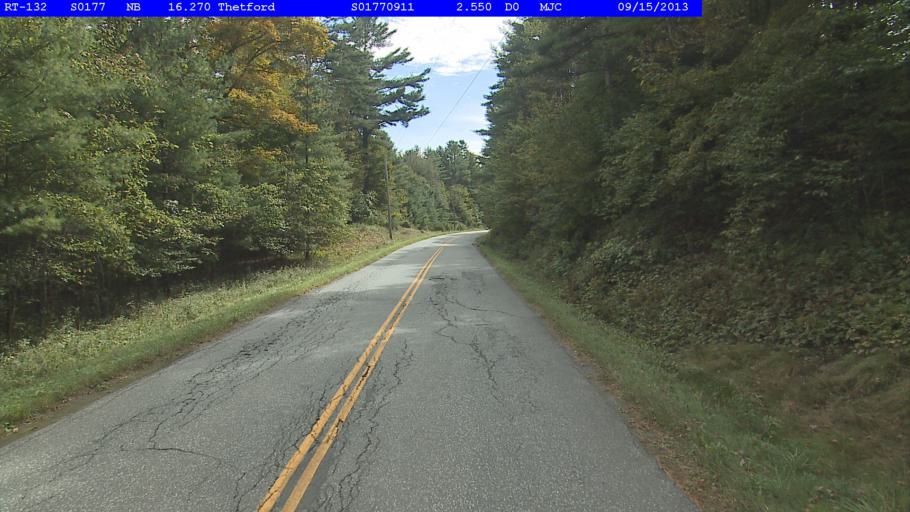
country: US
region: New Hampshire
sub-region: Grafton County
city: Hanover
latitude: 43.8200
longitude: -72.2812
